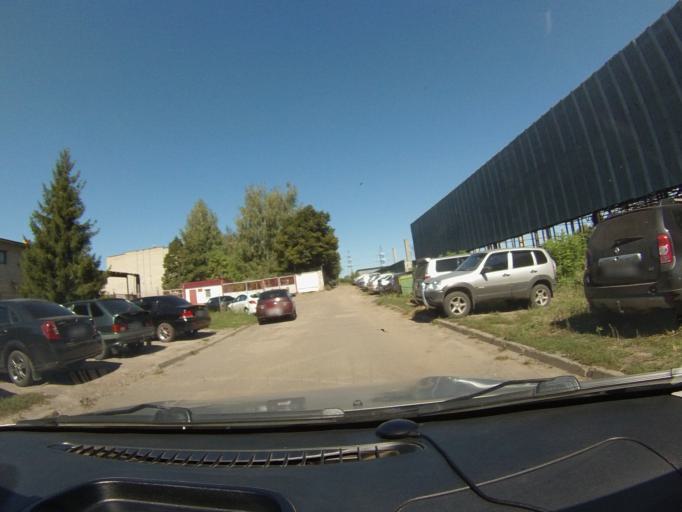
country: RU
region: Tambov
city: Tambov
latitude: 52.7600
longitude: 41.4329
